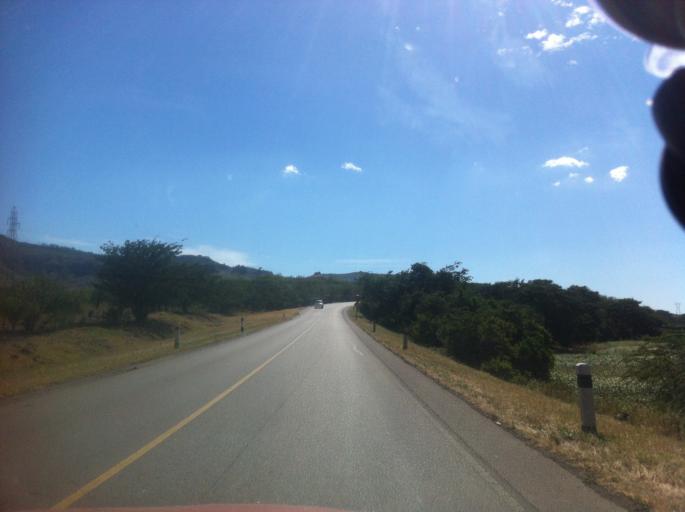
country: NI
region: Boaco
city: Teustepe
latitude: 12.4062
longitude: -85.8448
